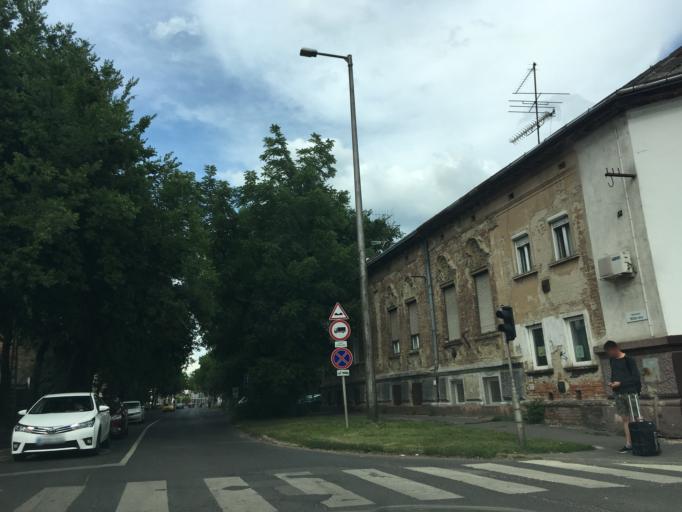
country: HU
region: Hajdu-Bihar
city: Debrecen
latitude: 47.5236
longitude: 21.6197
